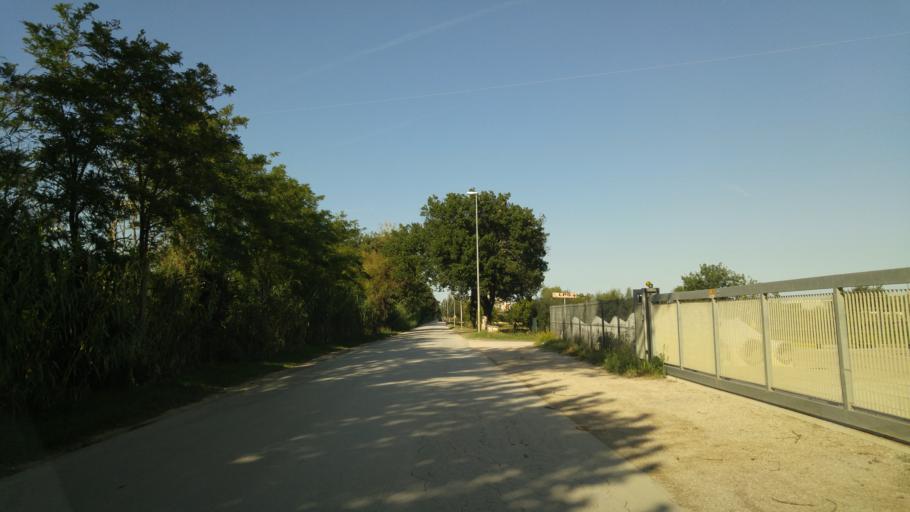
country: IT
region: The Marches
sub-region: Provincia di Pesaro e Urbino
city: Bellocchi
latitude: 43.7906
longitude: 13.0149
